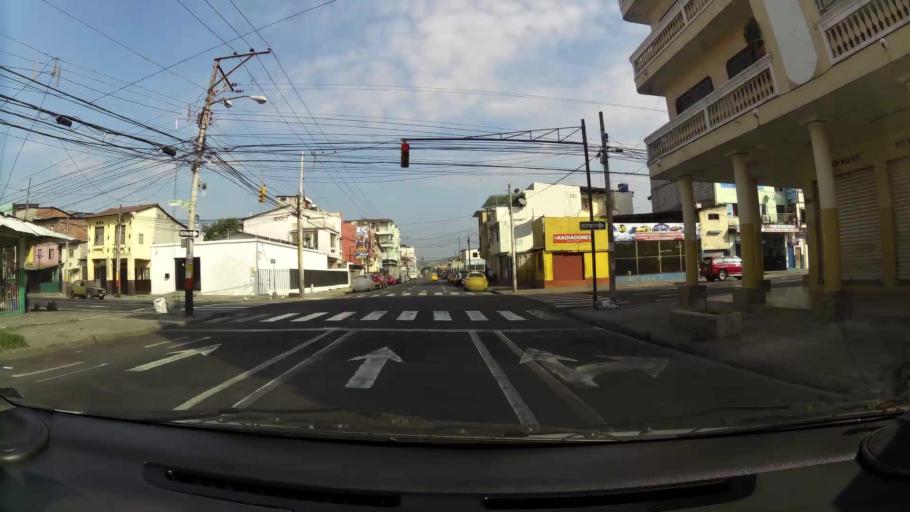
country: EC
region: Guayas
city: Guayaquil
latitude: -2.1969
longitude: -79.8983
